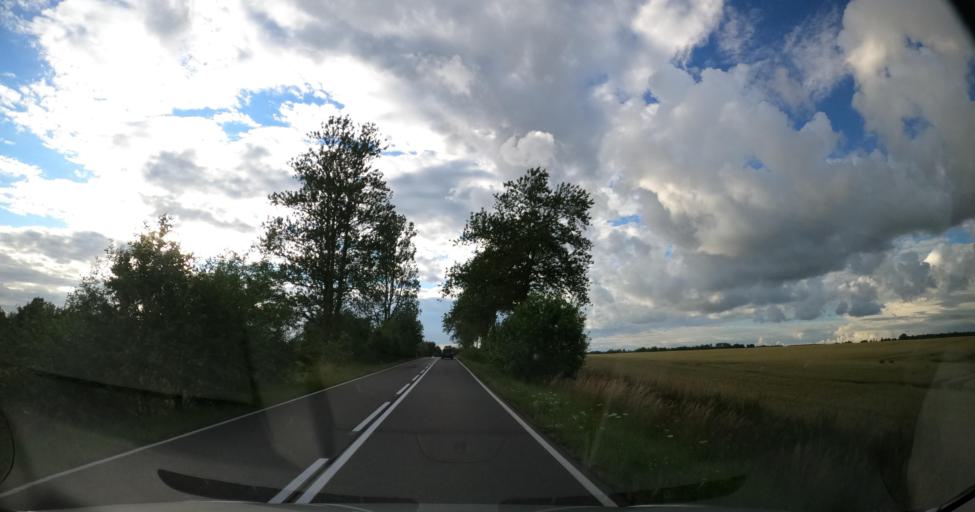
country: PL
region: Pomeranian Voivodeship
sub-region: Powiat slupski
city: Damnica
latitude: 54.4306
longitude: 17.3623
